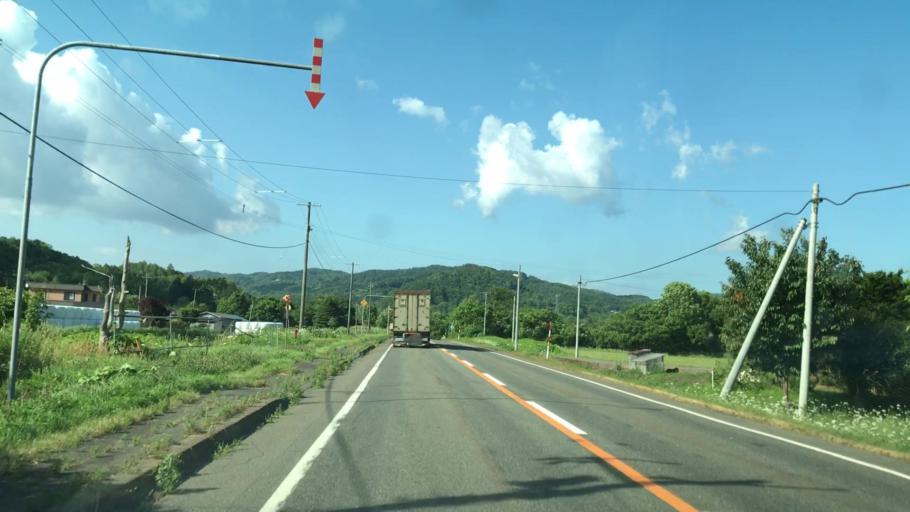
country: JP
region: Hokkaido
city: Shimo-furano
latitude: 42.8730
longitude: 142.4284
